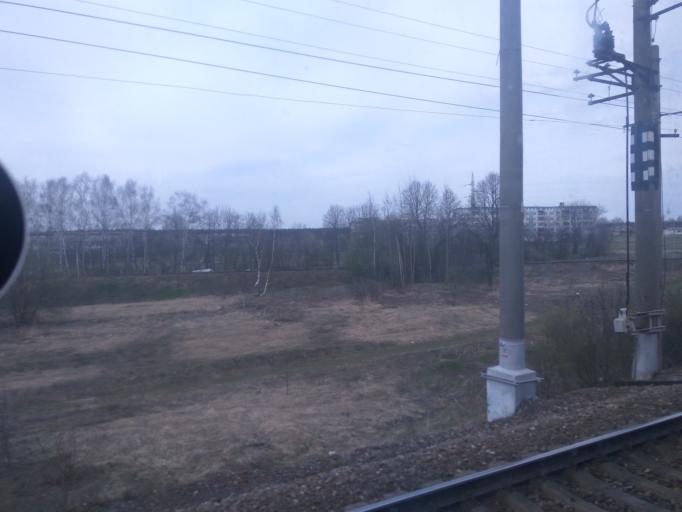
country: RU
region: Moskovskaya
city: Svatkovo
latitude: 56.3922
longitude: 38.2971
